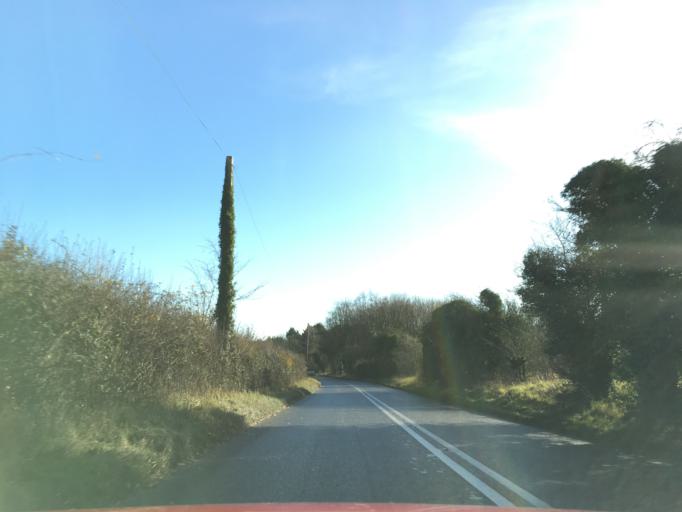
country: GB
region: England
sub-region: Wiltshire
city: Tidworth
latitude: 51.2591
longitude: -1.6351
